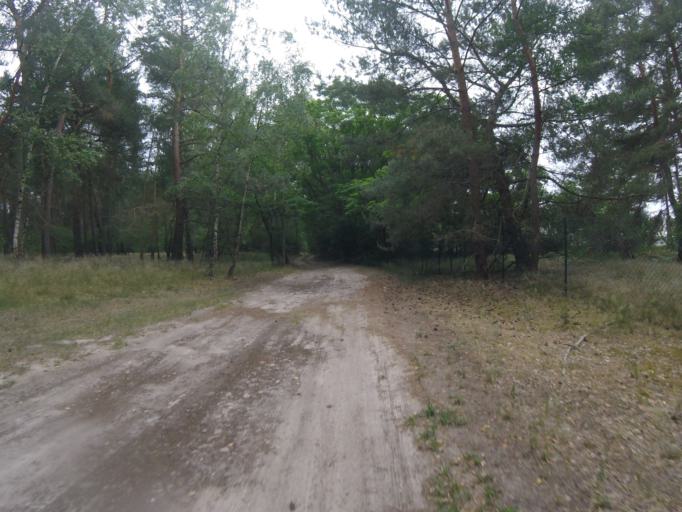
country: DE
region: Brandenburg
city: Bestensee
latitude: 52.2215
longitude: 13.6205
